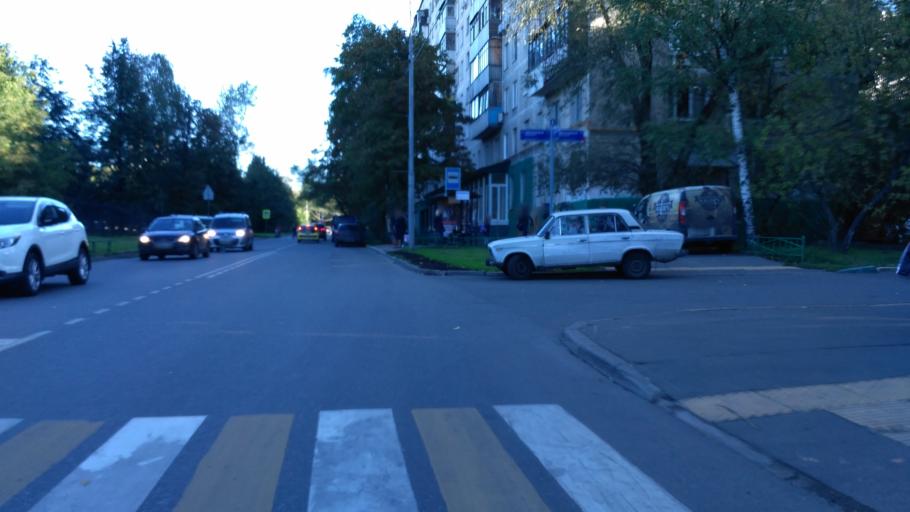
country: RU
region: Moscow
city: Zapadnoye Degunino
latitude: 55.8835
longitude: 37.5328
